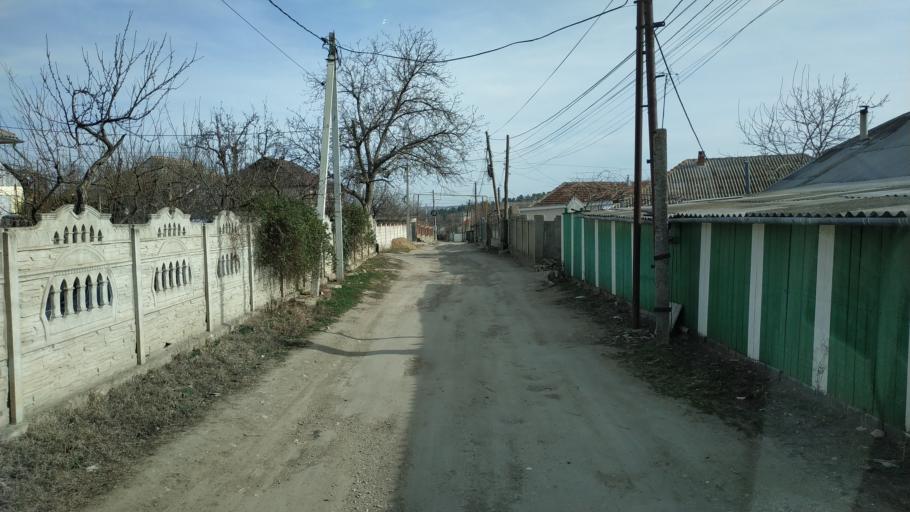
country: MD
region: Chisinau
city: Vatra
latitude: 47.0746
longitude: 28.6827
